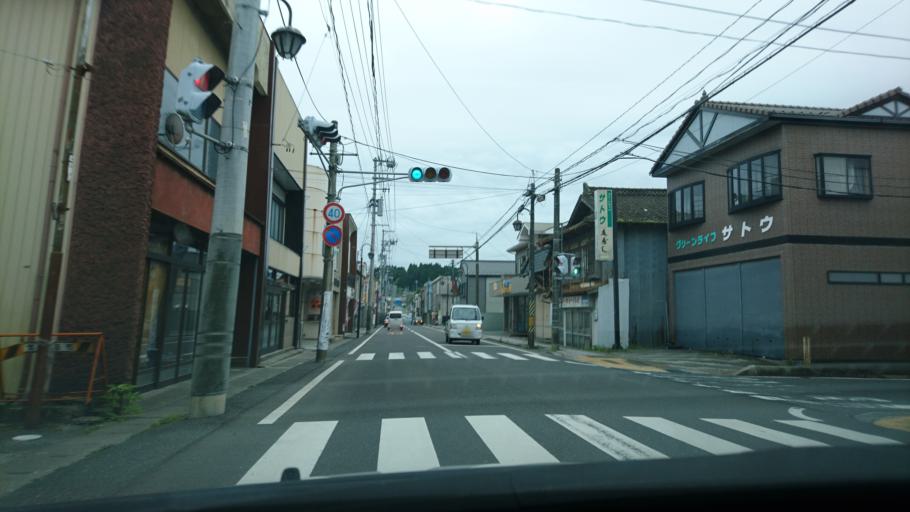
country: JP
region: Iwate
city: Ofunato
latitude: 38.7922
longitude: 141.5047
